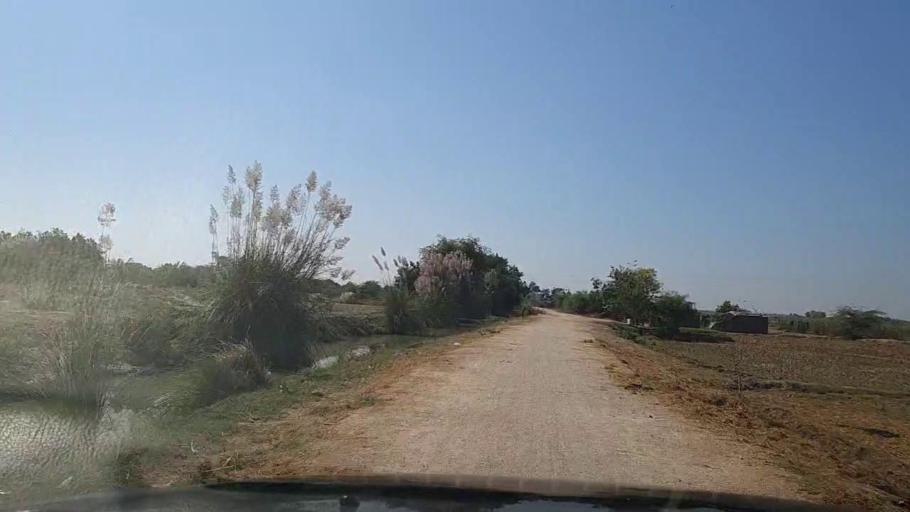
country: PK
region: Sindh
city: Thatta
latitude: 24.5896
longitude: 67.8180
